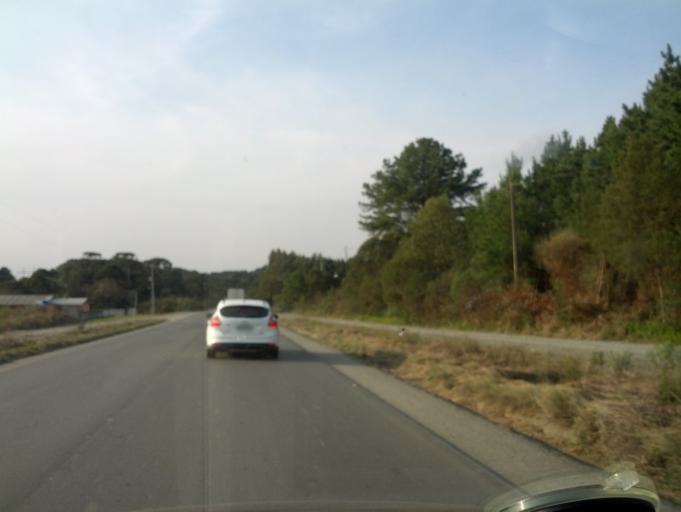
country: BR
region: Santa Catarina
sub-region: Otacilio Costa
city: Otacilio Costa
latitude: -27.5372
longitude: -50.1436
